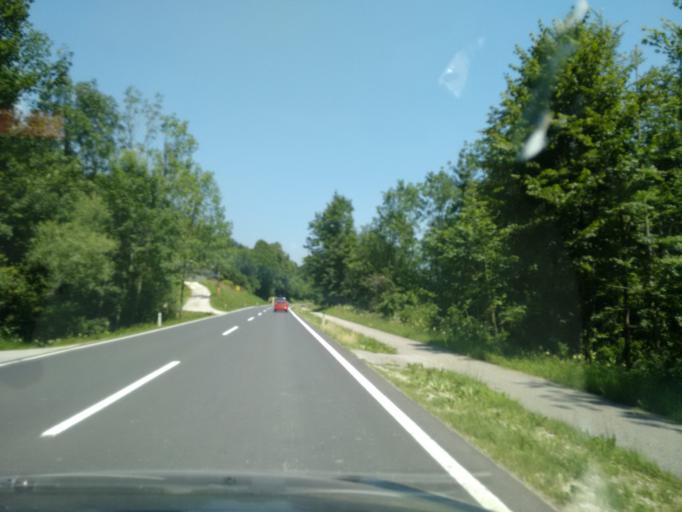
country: AT
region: Upper Austria
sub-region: Politischer Bezirk Gmunden
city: Ebensee
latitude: 47.7605
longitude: 13.7067
